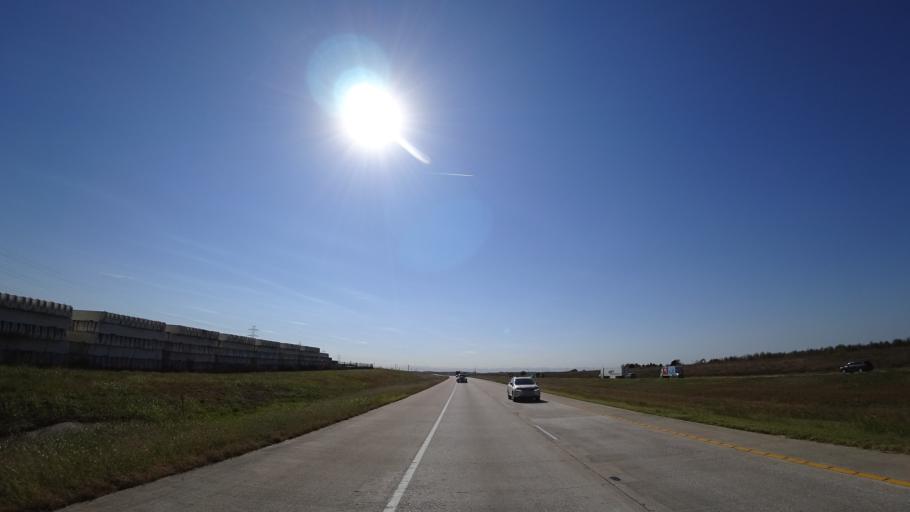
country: US
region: Texas
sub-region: Travis County
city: Manor
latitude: 30.3819
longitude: -97.5798
